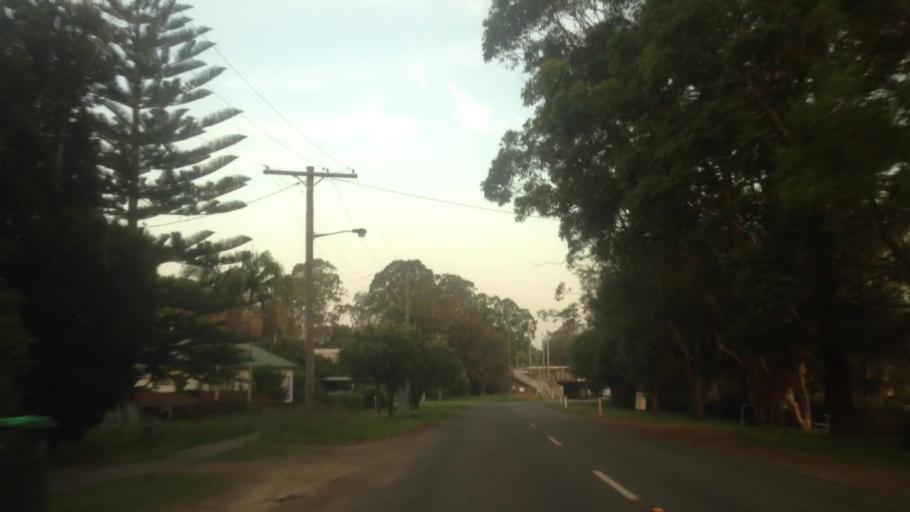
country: AU
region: New South Wales
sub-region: Lake Macquarie Shire
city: Dora Creek
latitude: -33.0829
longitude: 151.4993
